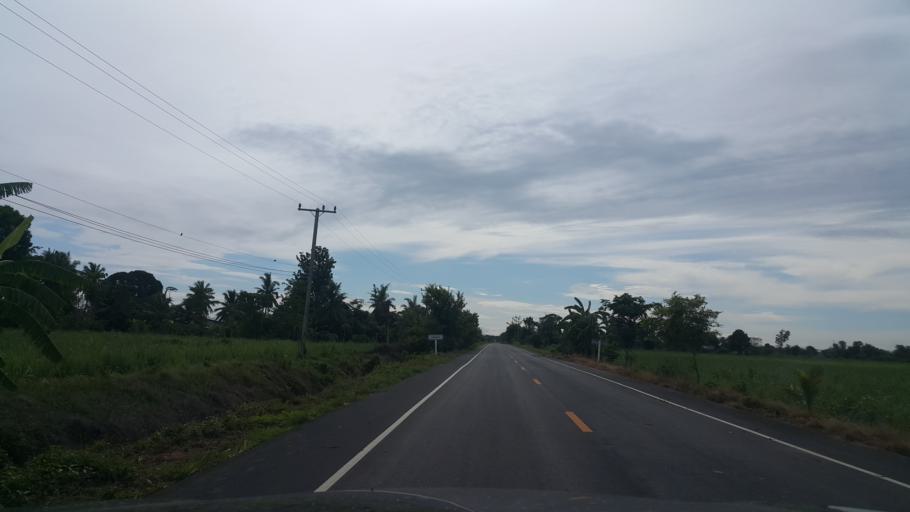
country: TH
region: Sukhothai
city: Si Nakhon
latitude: 17.2708
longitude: 99.9392
